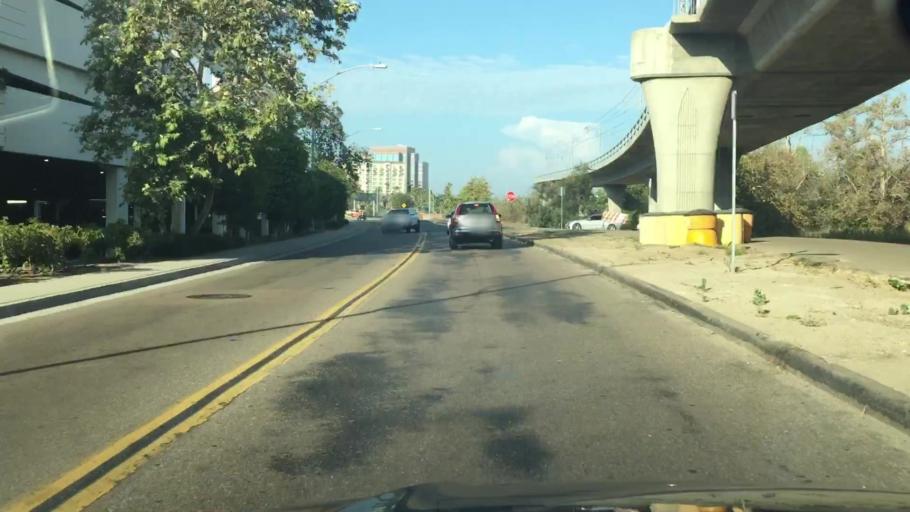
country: US
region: California
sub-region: San Diego County
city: San Diego
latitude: 32.7666
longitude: -117.1652
